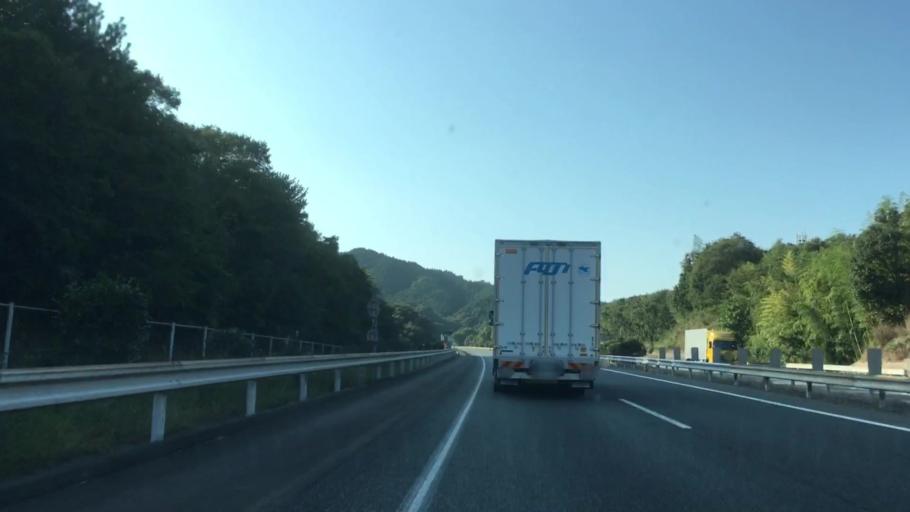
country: JP
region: Yamaguchi
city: Hofu
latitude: 34.0753
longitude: 131.4926
